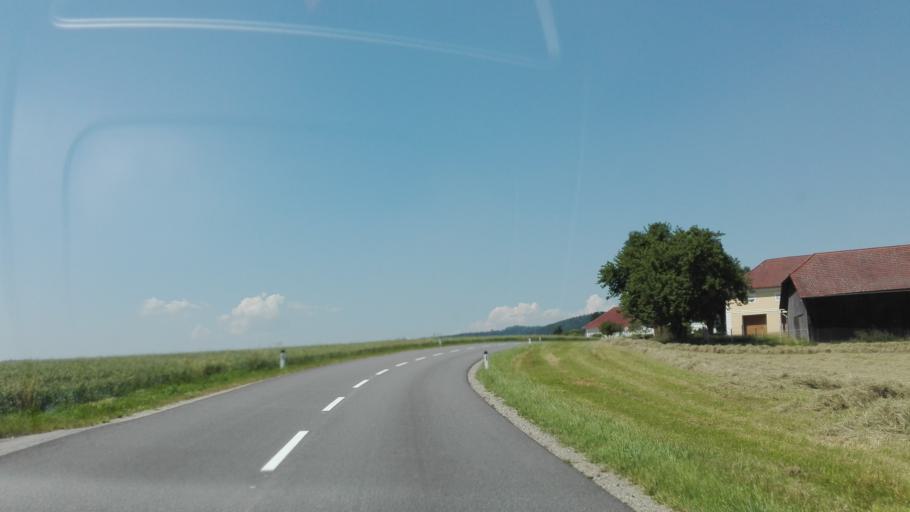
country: AT
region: Upper Austria
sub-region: Politischer Bezirk Grieskirchen
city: Grieskirchen
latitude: 48.3571
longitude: 13.8622
